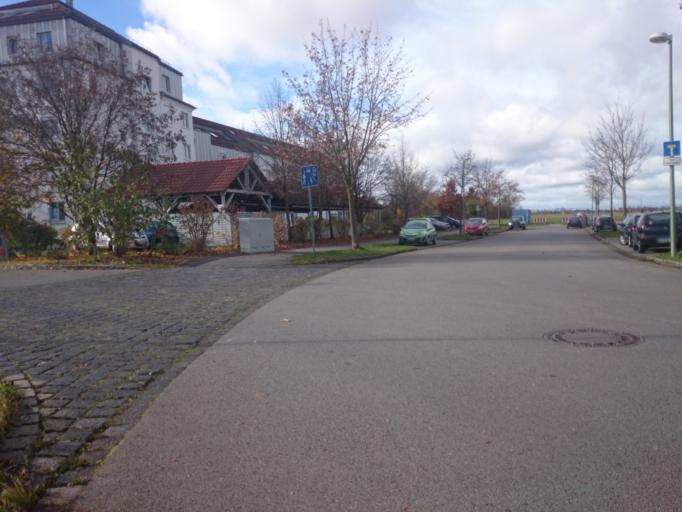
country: DE
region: Bavaria
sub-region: Swabia
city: Konigsbrunn
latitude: 48.3001
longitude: 10.8978
